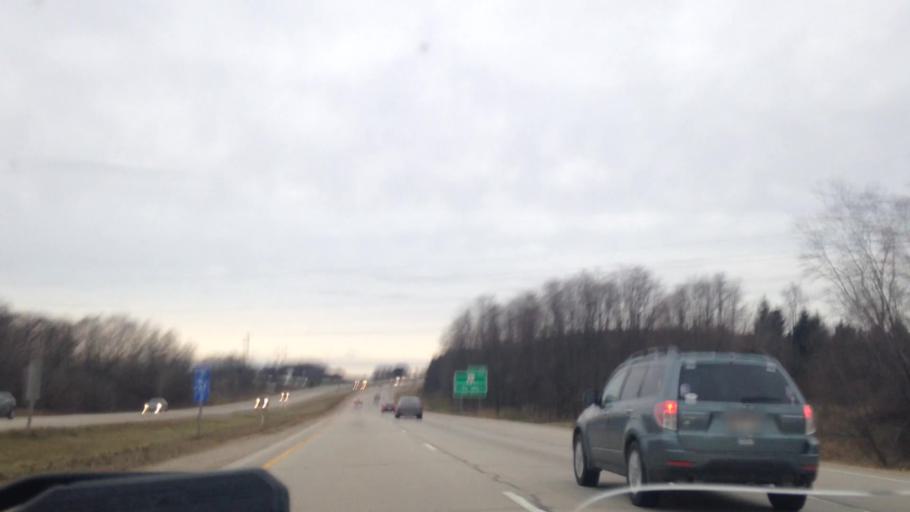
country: US
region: Wisconsin
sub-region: Washington County
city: Slinger
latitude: 43.3530
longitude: -88.2867
